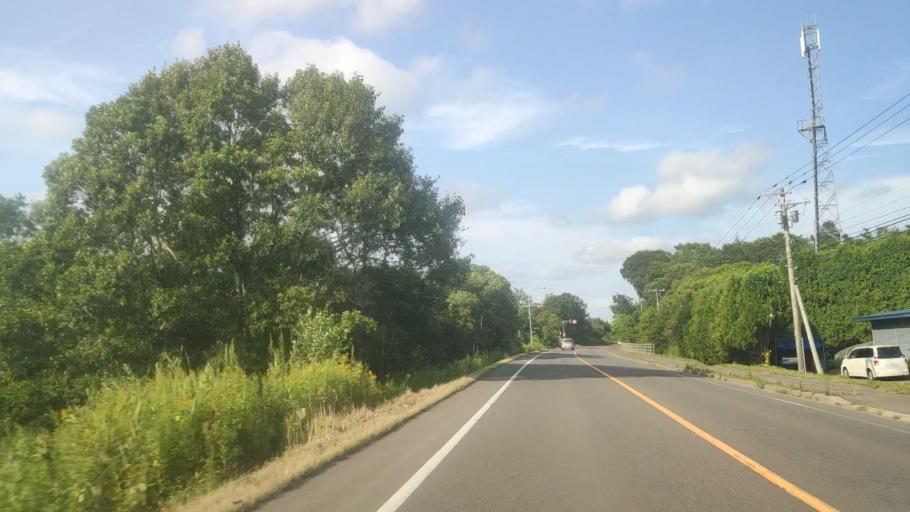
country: JP
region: Hokkaido
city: Chitose
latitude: 42.7336
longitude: 141.7761
